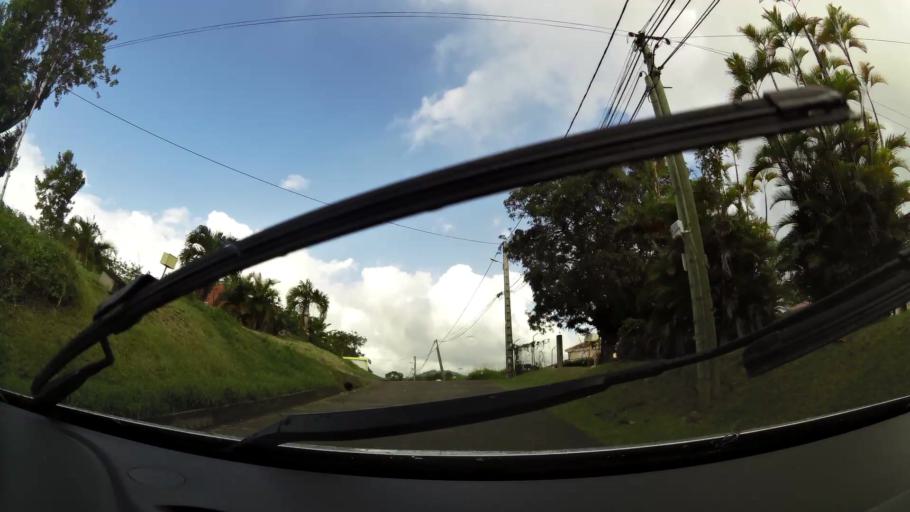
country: MQ
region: Martinique
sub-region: Martinique
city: Saint-Esprit
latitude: 14.5067
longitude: -60.9630
